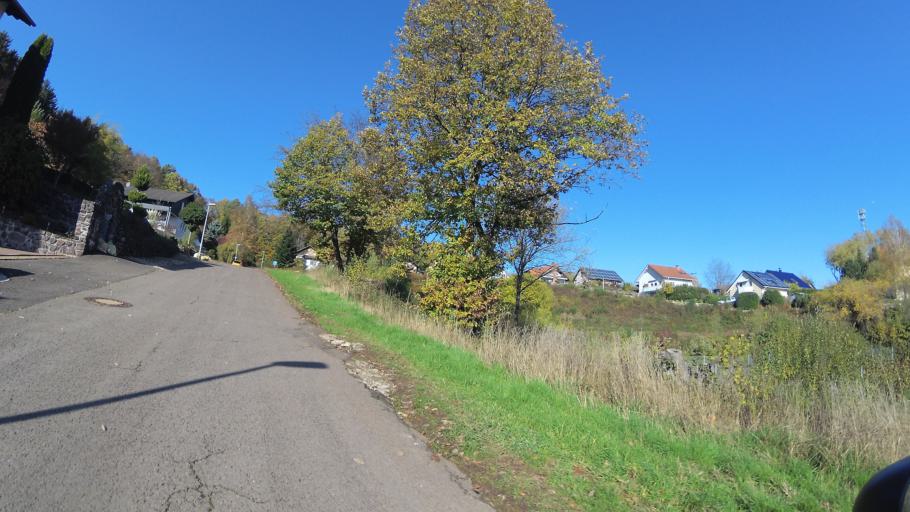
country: DE
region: Saarland
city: Losheim
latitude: 49.5439
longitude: 6.7728
